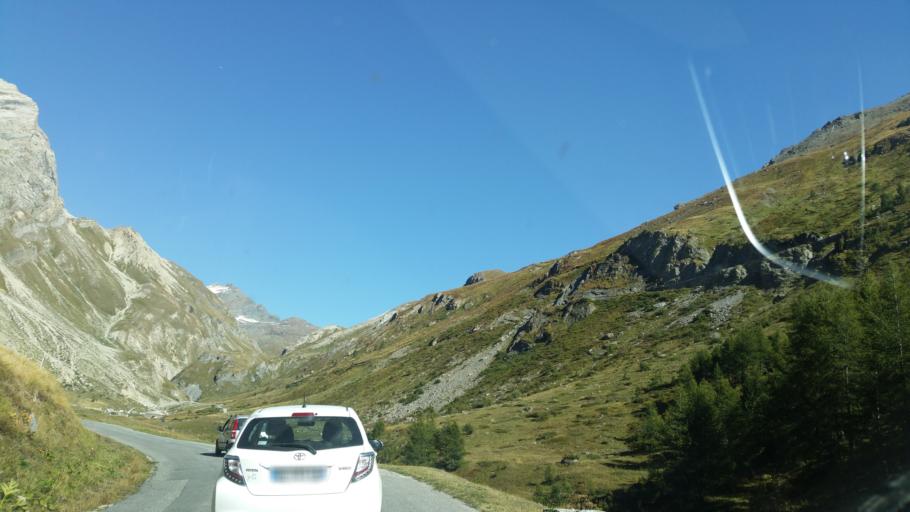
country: FR
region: Rhone-Alpes
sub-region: Departement de la Savoie
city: Val-d'Isere
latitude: 45.4514
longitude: 7.0240
